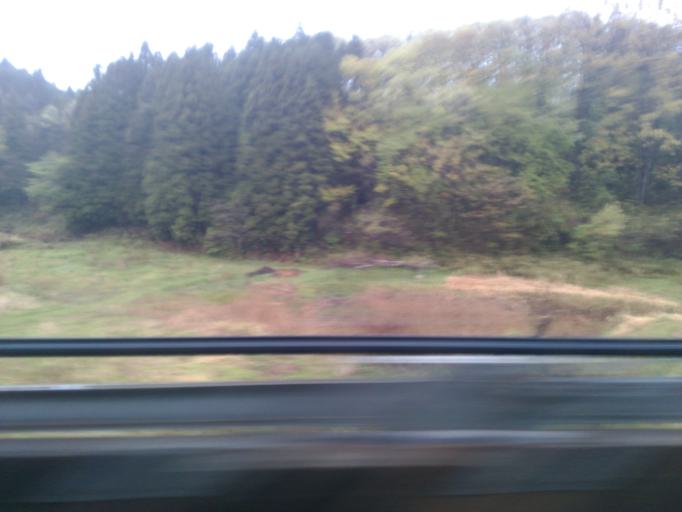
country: JP
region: Miyagi
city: Okawara
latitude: 38.0702
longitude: 140.7262
